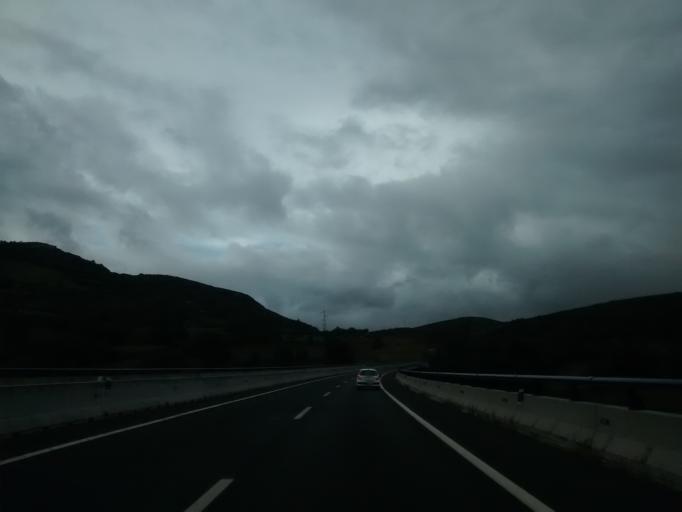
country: ES
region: Cantabria
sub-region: Provincia de Cantabria
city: Arenas de Iguna
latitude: 43.1938
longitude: -4.0705
